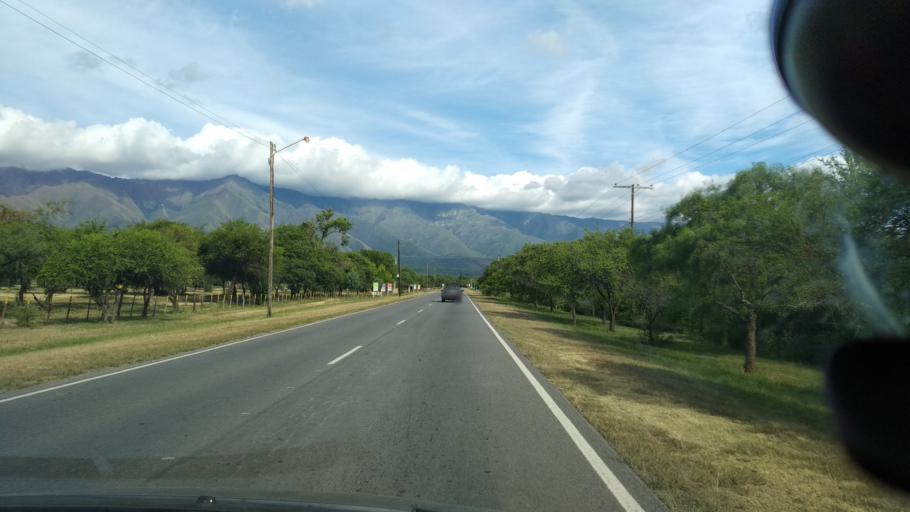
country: AR
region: Cordoba
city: Villa Las Rosas
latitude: -32.0075
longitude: -65.0575
